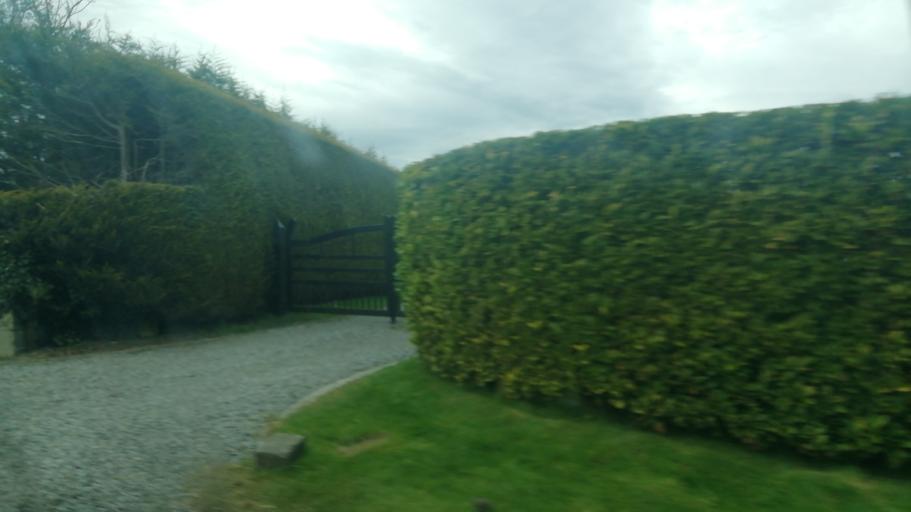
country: IE
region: Leinster
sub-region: Kildare
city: Clane
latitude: 53.3117
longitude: -6.7163
